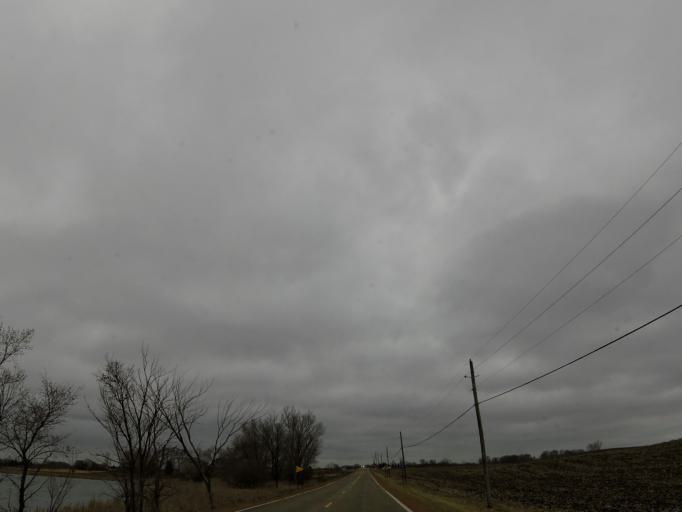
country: US
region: Minnesota
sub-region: Scott County
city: Shakopee
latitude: 44.7356
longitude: -93.5420
